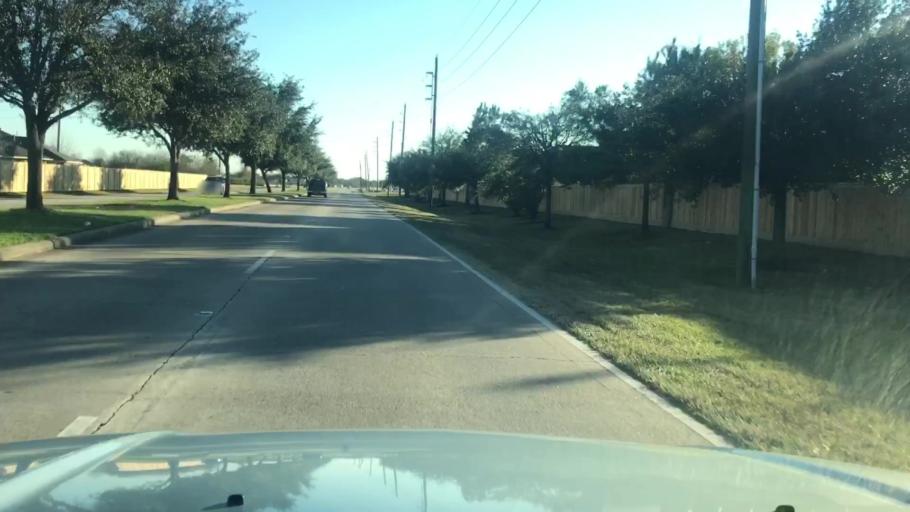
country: US
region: Texas
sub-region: Fort Bend County
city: Cinco Ranch
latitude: 29.8414
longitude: -95.7189
